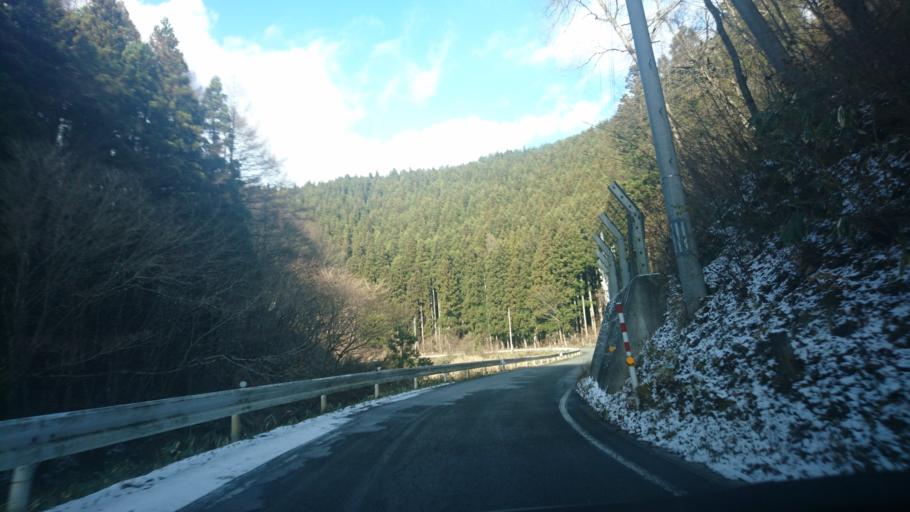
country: JP
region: Iwate
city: Mizusawa
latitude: 39.0974
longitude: 141.3838
